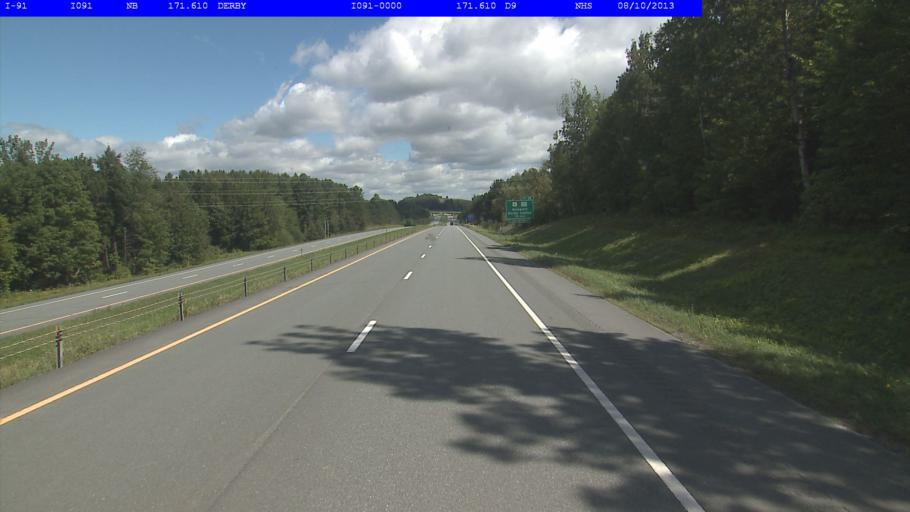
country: US
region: Vermont
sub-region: Orleans County
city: Newport
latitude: 44.9423
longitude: -72.1581
